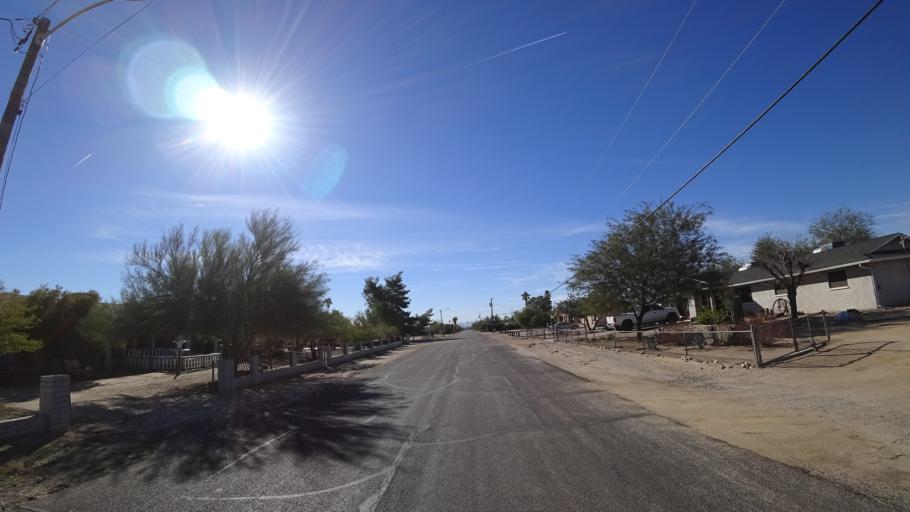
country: US
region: Arizona
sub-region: Maricopa County
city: Citrus Park
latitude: 33.4711
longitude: -112.4897
